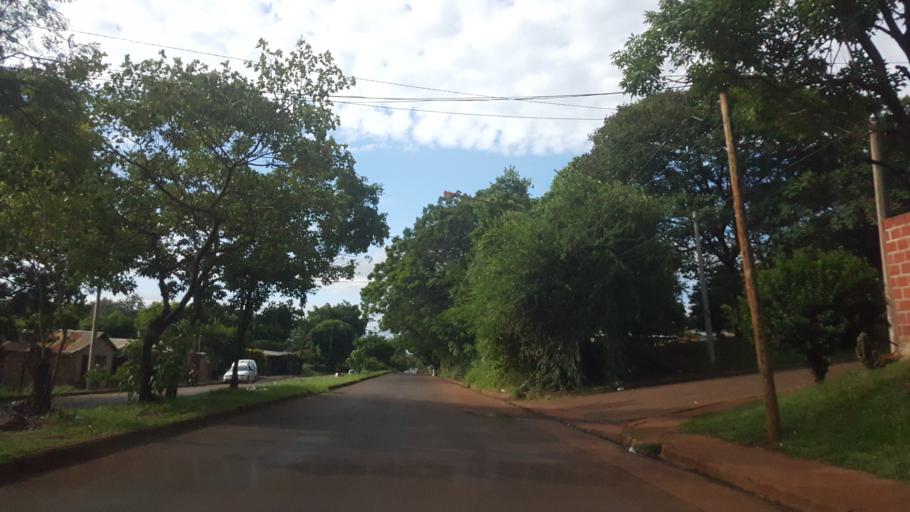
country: AR
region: Misiones
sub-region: Departamento de Capital
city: Posadas
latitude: -27.3798
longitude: -55.9334
